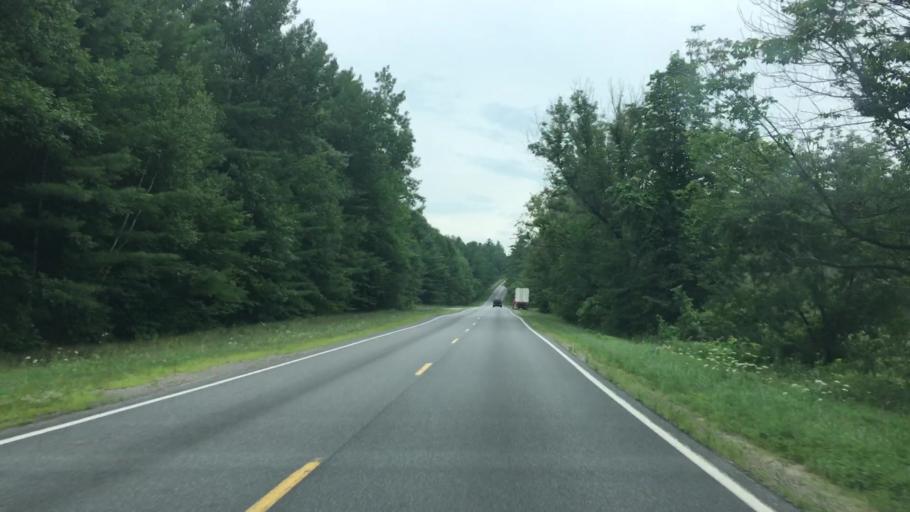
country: US
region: New York
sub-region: Clinton County
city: Peru
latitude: 44.4960
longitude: -73.5920
